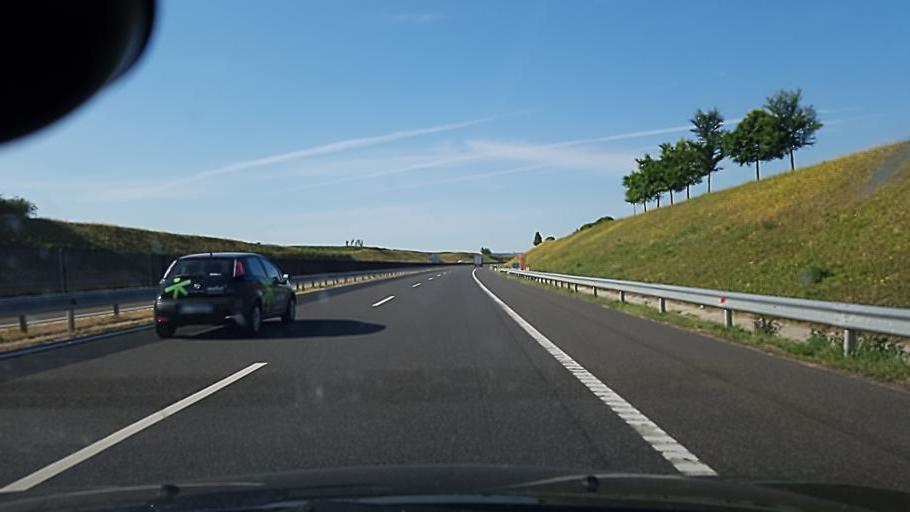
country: HU
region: Tolna
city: Madocsa
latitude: 46.7200
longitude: 18.8768
